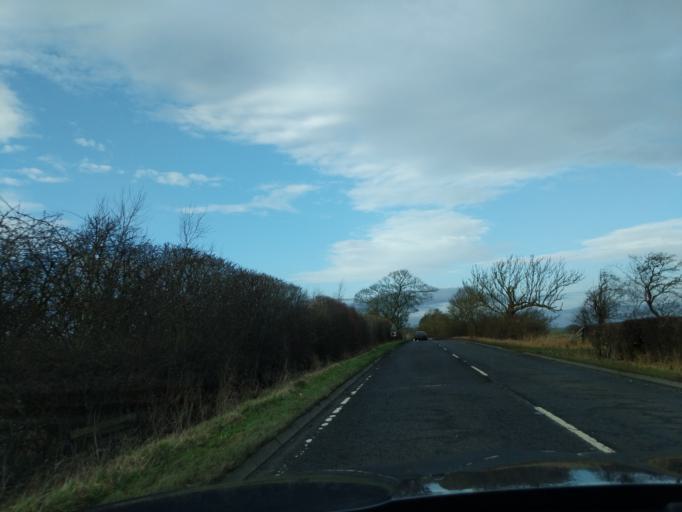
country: GB
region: England
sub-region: Northumberland
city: Darras Hall
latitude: 55.0607
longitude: -1.7731
